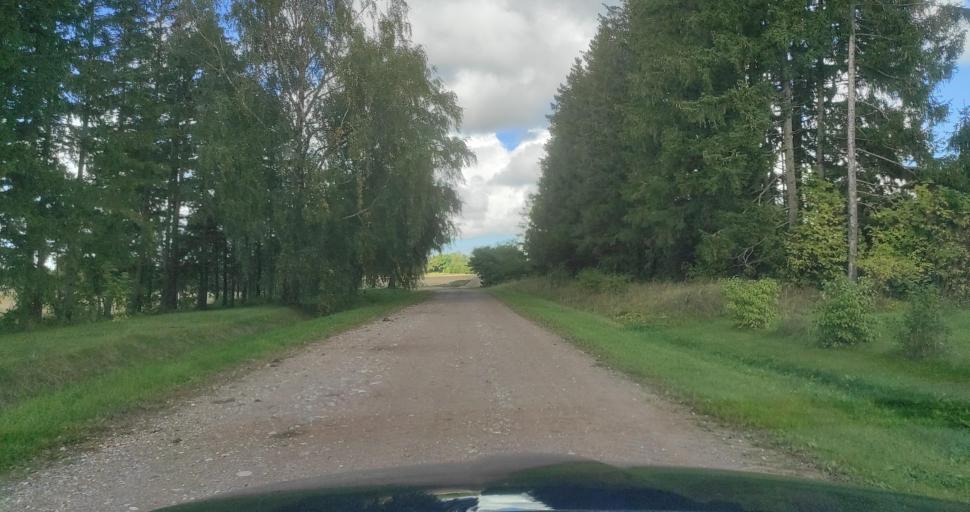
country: LV
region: Ventspils Rajons
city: Piltene
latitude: 57.2694
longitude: 21.5883
